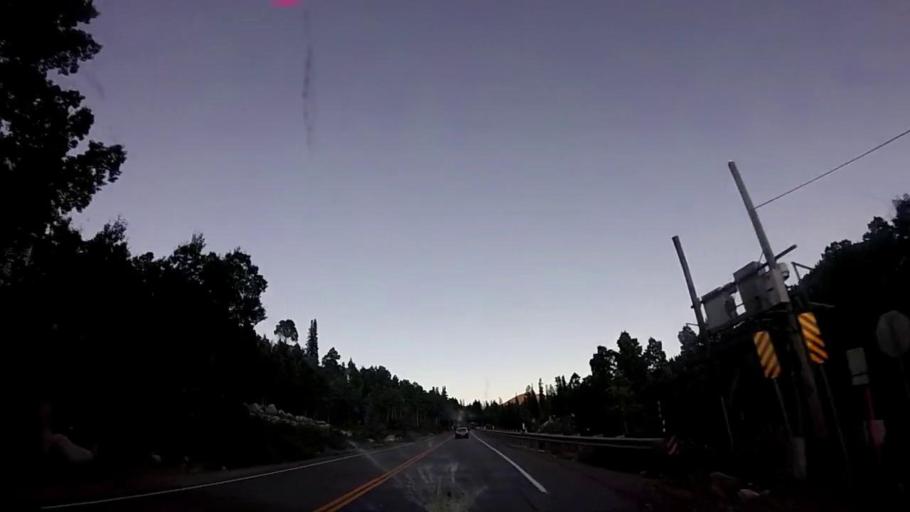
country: US
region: Utah
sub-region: Summit County
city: Snyderville
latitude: 40.6331
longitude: -111.6108
